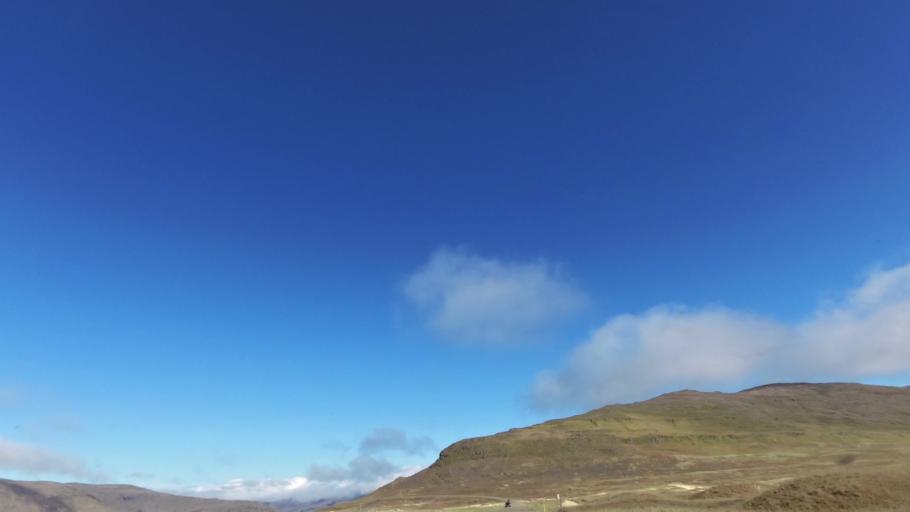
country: IS
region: West
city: Olafsvik
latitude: 65.5560
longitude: -23.9819
